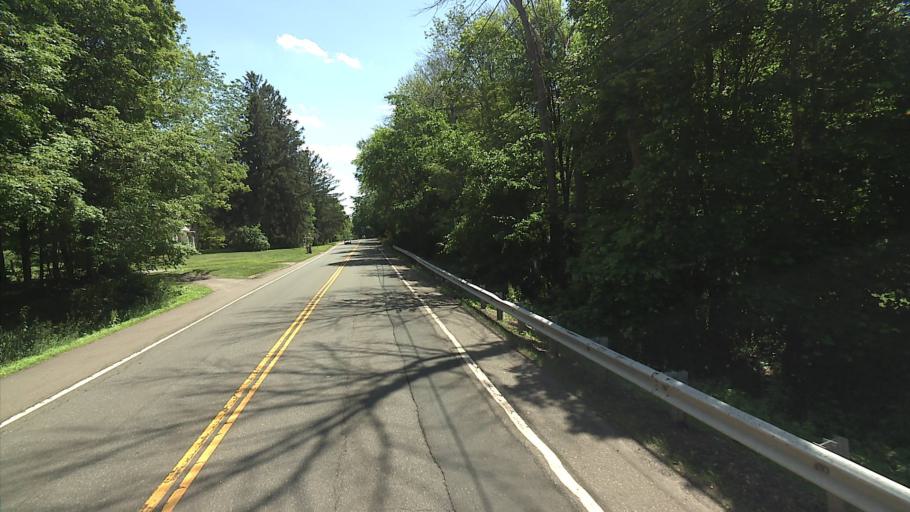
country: US
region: Connecticut
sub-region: New Haven County
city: Woodbridge
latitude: 41.3669
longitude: -72.9978
